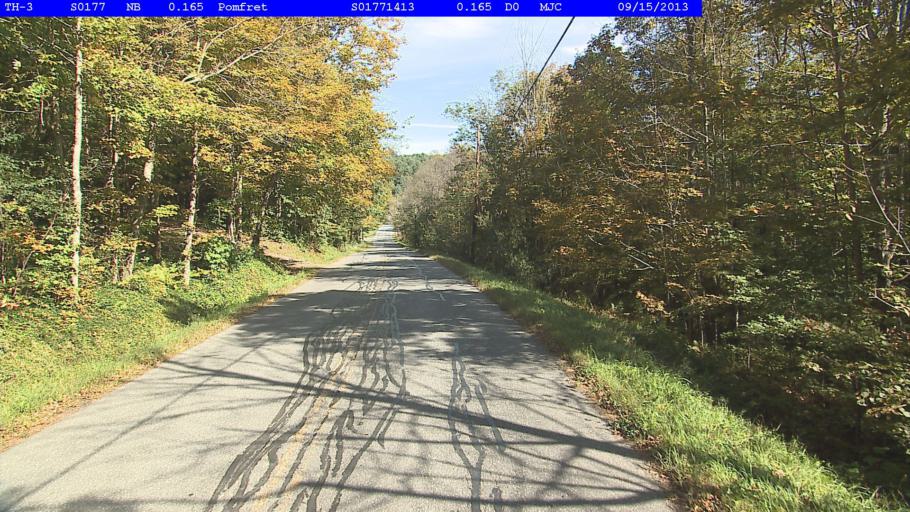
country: US
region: Vermont
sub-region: Windsor County
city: Woodstock
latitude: 43.7253
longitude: -72.4975
